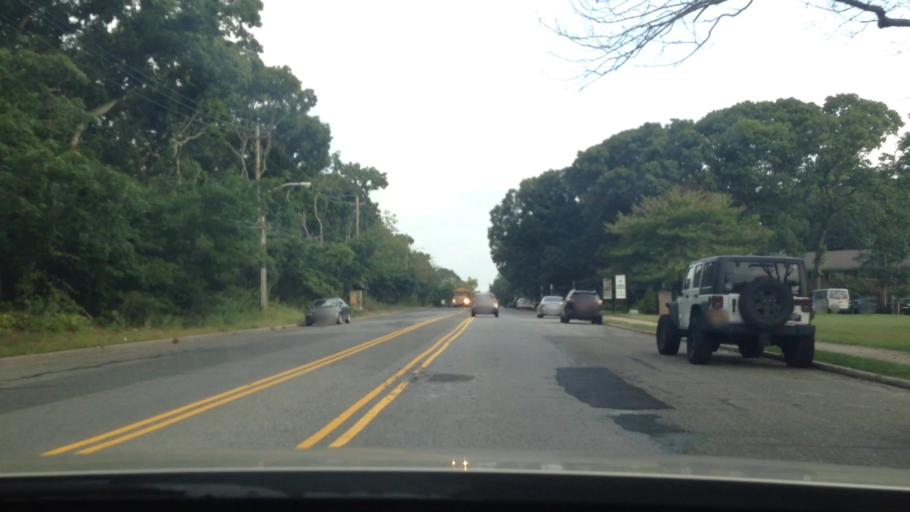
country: US
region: New York
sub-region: Suffolk County
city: Selden
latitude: 40.8532
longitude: -73.0459
